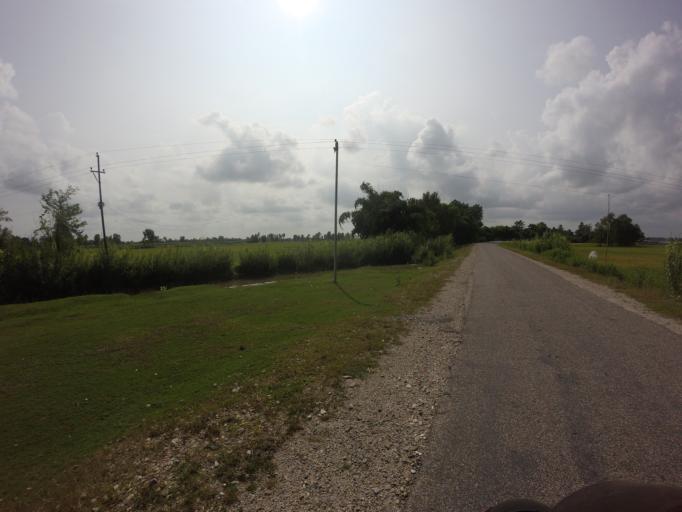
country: NP
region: Far Western
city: Tikapur
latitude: 28.4702
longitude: 81.0732
